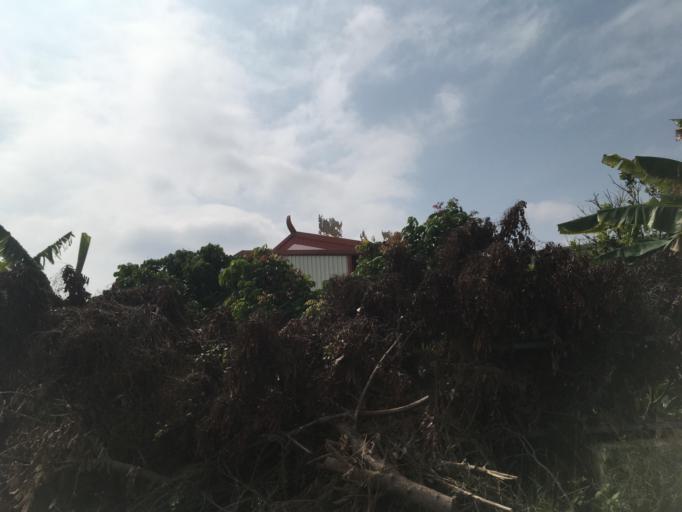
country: TW
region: Taiwan
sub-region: Yunlin
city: Douliu
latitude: 23.6893
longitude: 120.4622
